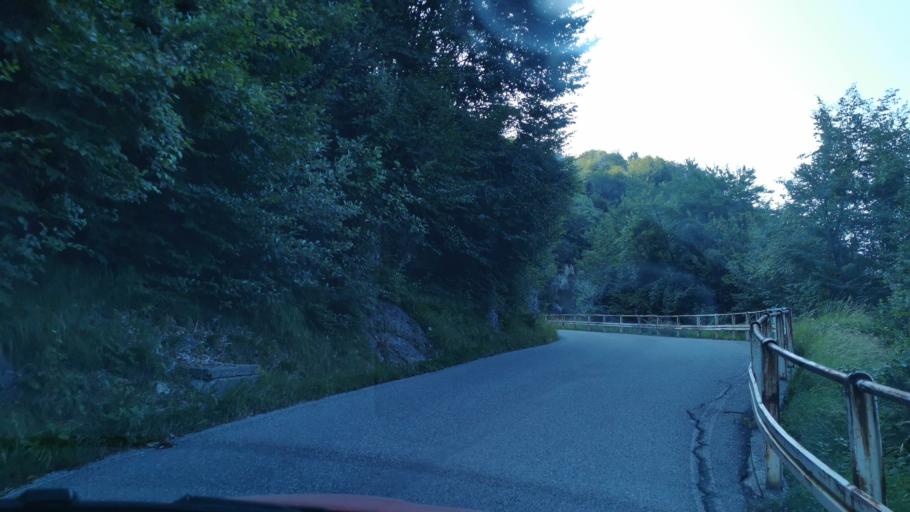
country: IT
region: Lombardy
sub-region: Provincia di Lecco
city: Moggio
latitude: 45.9170
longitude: 9.4929
